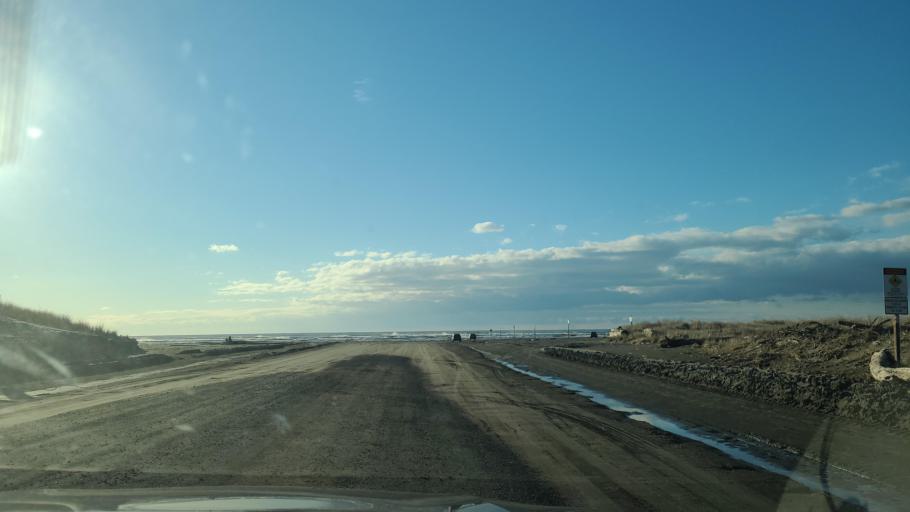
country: US
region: Washington
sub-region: Grays Harbor County
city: Ocean Shores
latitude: 46.9940
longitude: -124.1720
